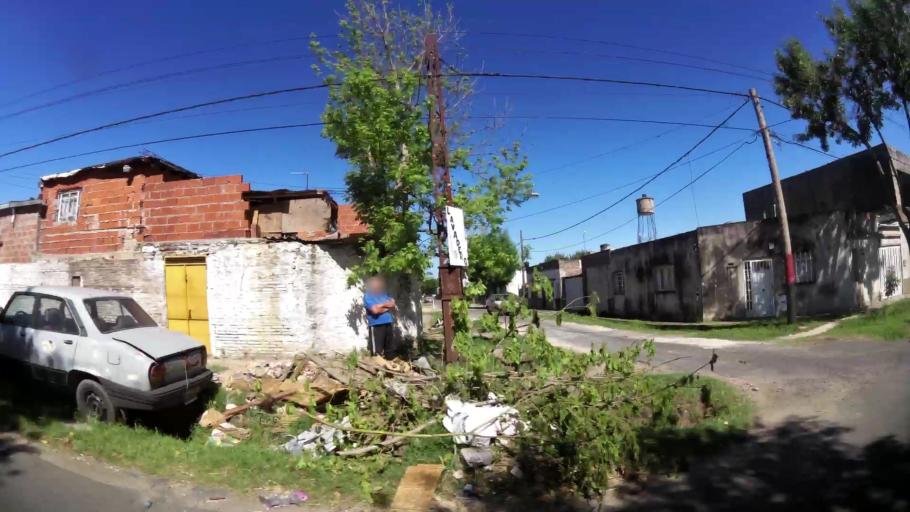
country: AR
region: Santa Fe
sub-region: Departamento de Rosario
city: Rosario
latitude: -32.9618
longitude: -60.6939
